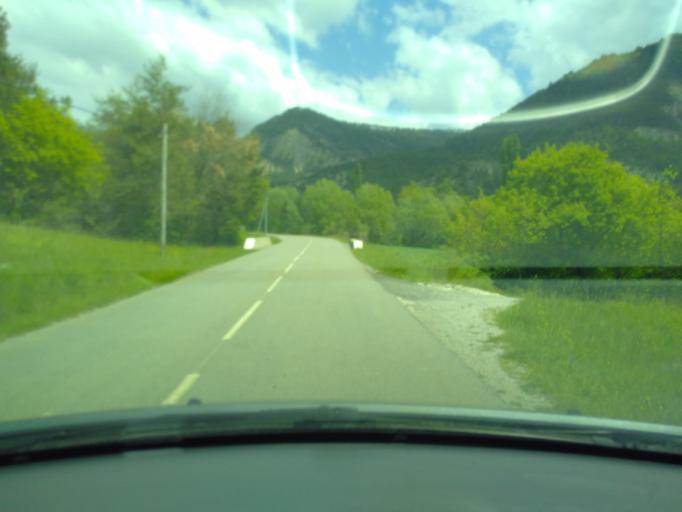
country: FR
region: Rhone-Alpes
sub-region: Departement de la Drome
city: Die
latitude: 44.6515
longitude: 5.4633
